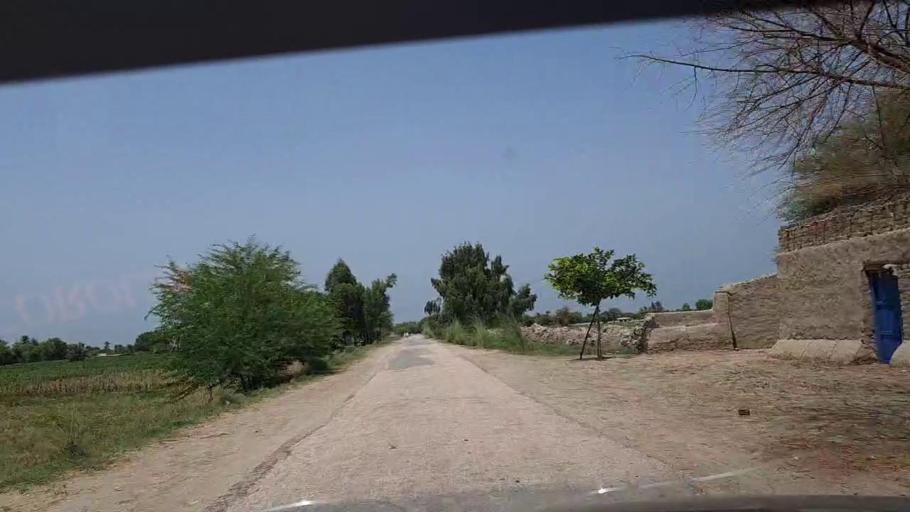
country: PK
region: Sindh
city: Khanpur
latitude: 27.8069
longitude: 69.4506
